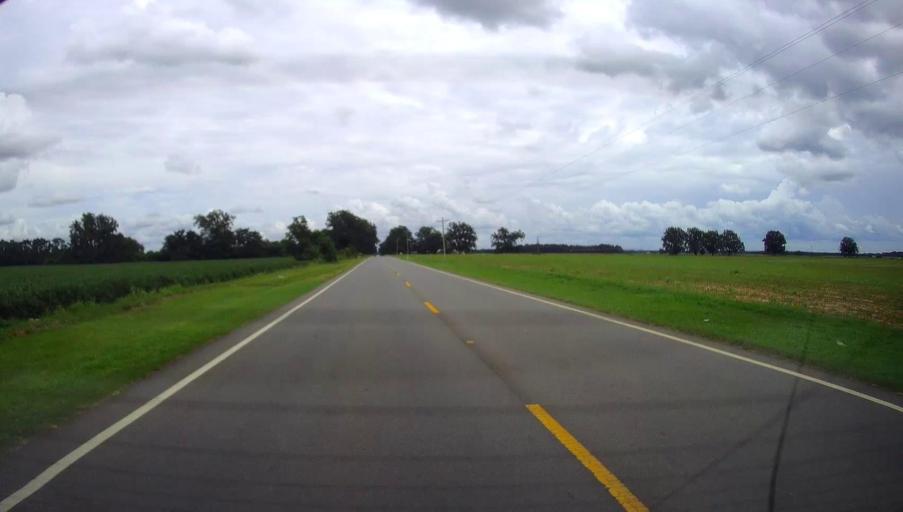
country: US
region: Georgia
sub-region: Macon County
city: Montezuma
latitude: 32.2931
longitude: -83.9771
